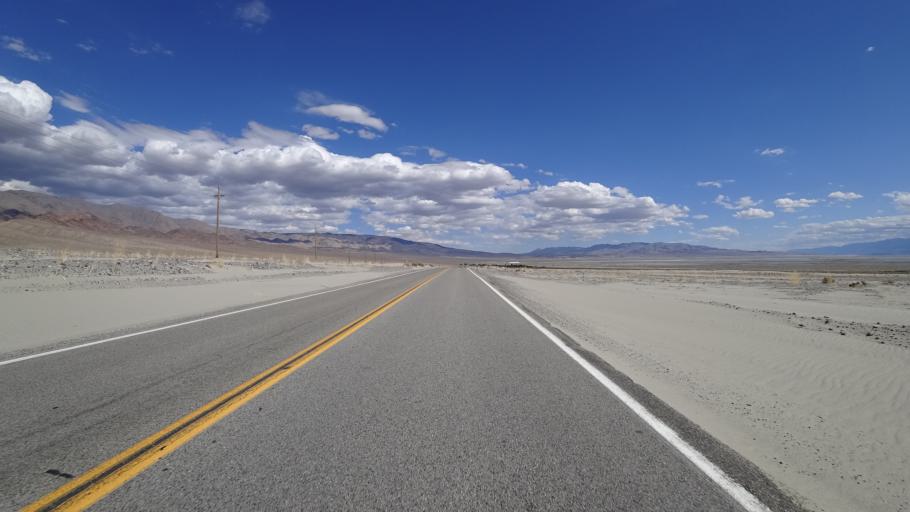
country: US
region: California
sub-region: Inyo County
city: Lone Pine
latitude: 36.5055
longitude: -117.8881
